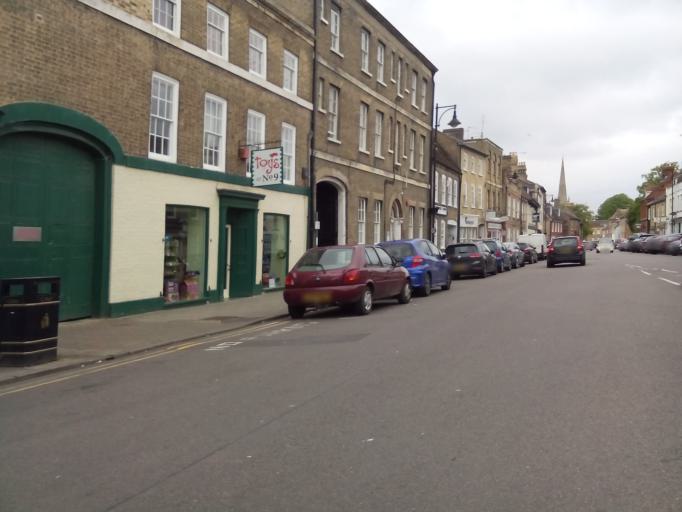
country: GB
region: England
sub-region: Cambridgeshire
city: Hemingford Grey
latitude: 52.3243
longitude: -0.0751
